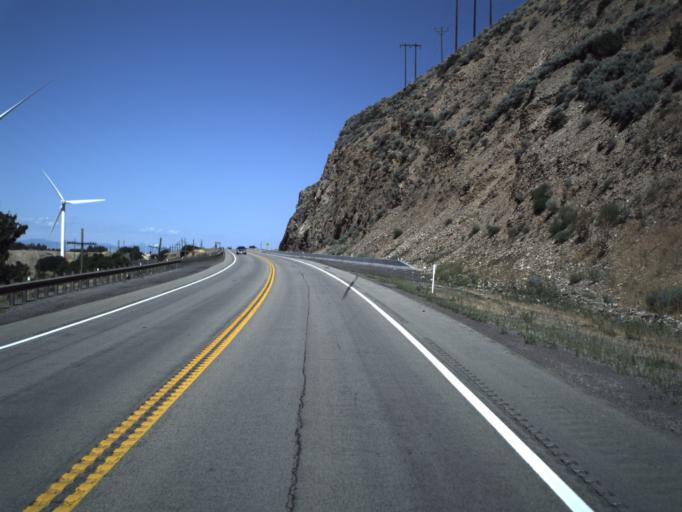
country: US
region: Utah
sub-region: Utah County
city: Mapleton
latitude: 40.0700
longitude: -111.5757
